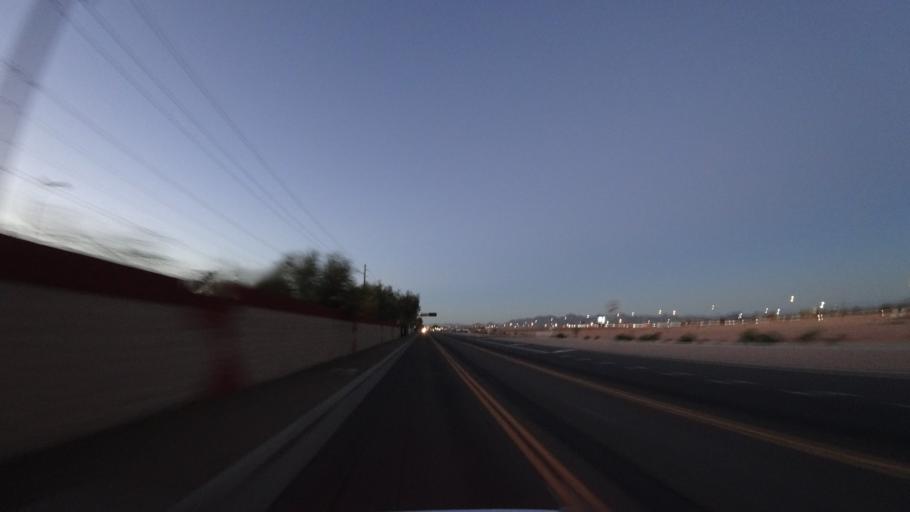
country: US
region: Arizona
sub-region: Maricopa County
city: Scottsdale
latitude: 33.4867
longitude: -111.8918
